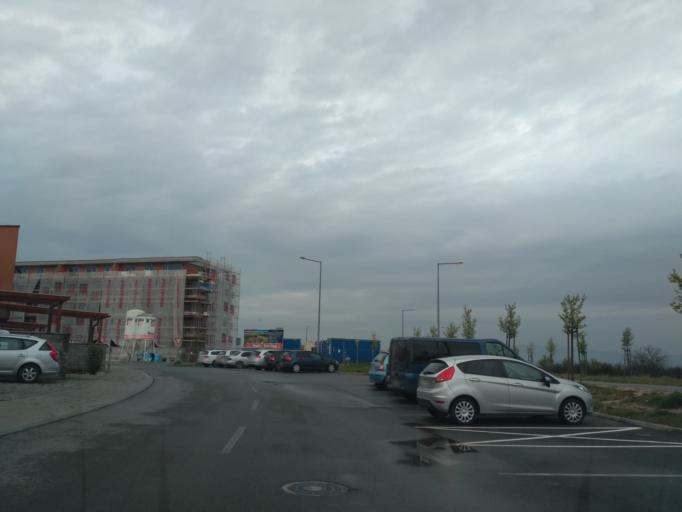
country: SK
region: Kosicky
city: Kosice
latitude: 48.7210
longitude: 21.2953
